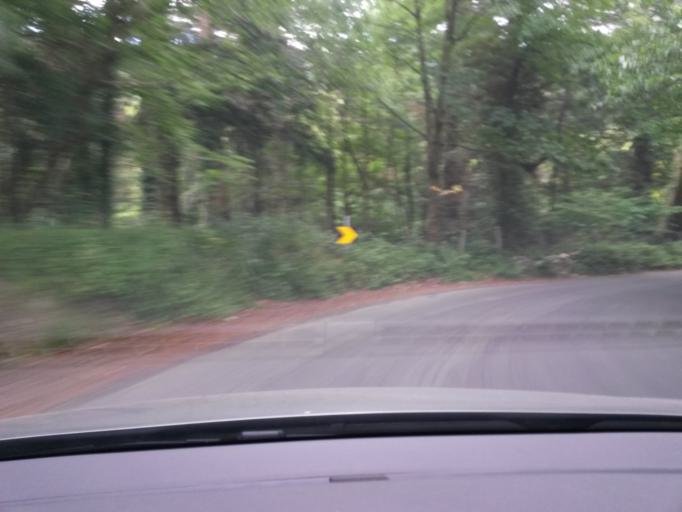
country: IE
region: Leinster
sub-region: Wicklow
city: Enniskerry
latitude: 53.1587
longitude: -6.1965
